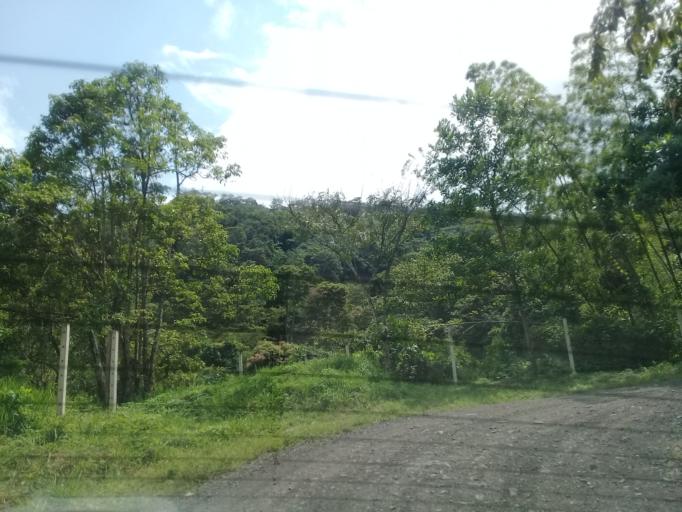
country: CO
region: Cundinamarca
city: Viani
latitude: 4.8605
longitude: -74.5403
